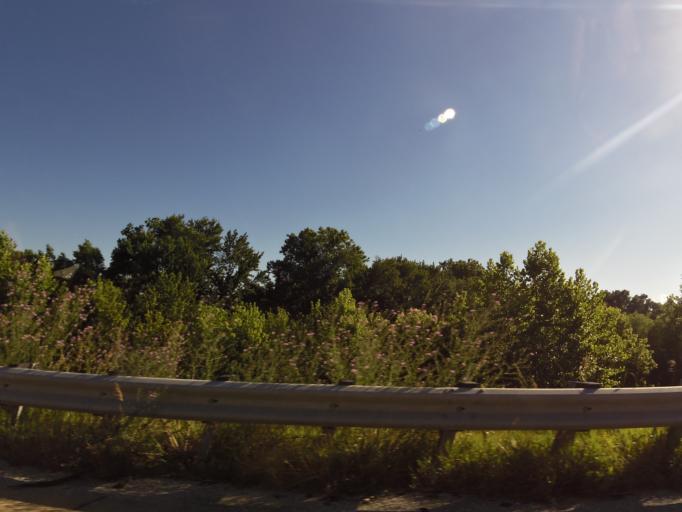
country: US
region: Missouri
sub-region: Ralls County
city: New London
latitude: 39.5209
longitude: -91.3440
